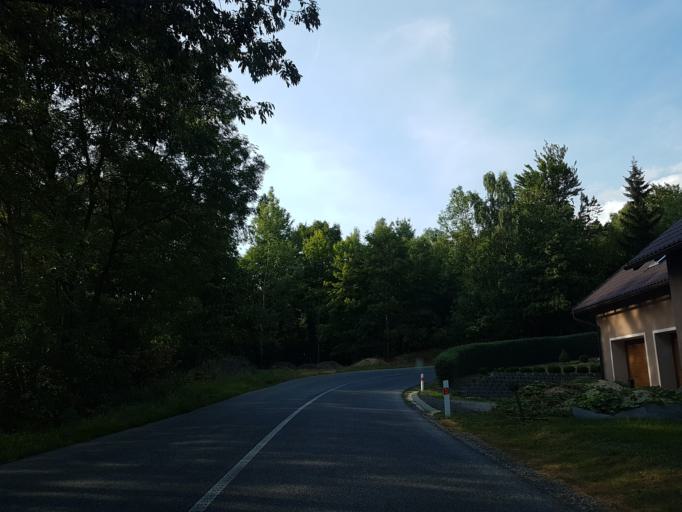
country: CZ
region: Liberecky
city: Mala Skala
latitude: 50.6582
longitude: 15.1561
